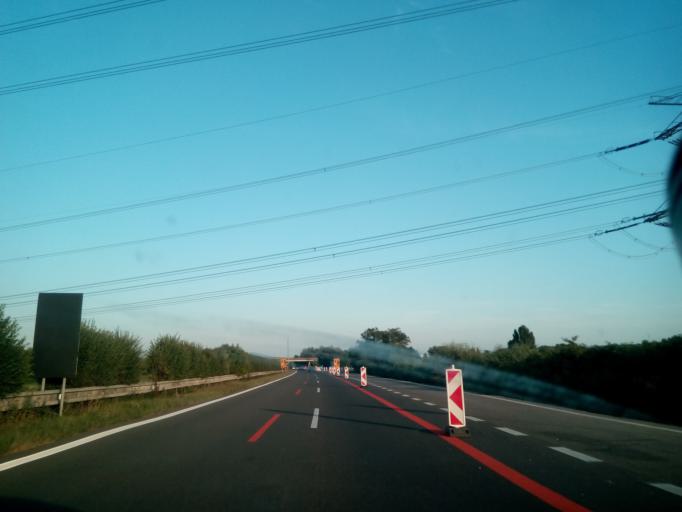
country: SK
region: Presovsky
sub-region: Okres Presov
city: Presov
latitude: 48.8602
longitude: 21.2646
